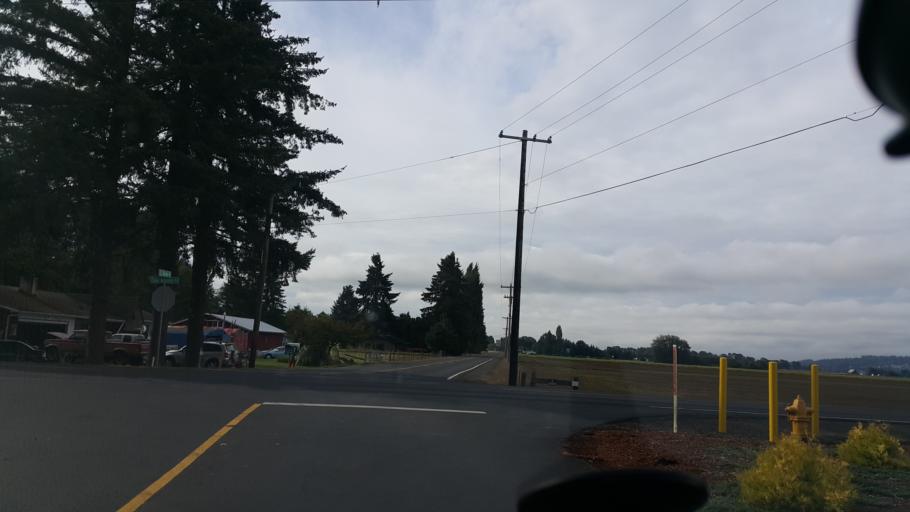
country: US
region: Washington
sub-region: Cowlitz County
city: Woodland
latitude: 45.9279
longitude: -122.7684
